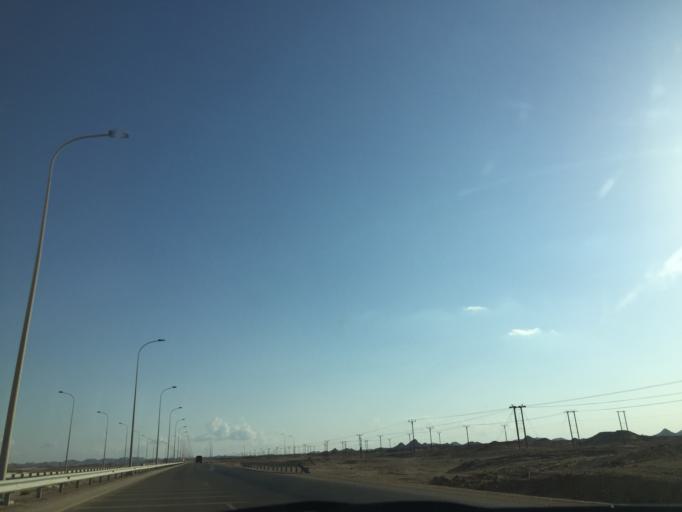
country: OM
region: Zufar
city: Salalah
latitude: 17.5348
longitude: 54.0555
